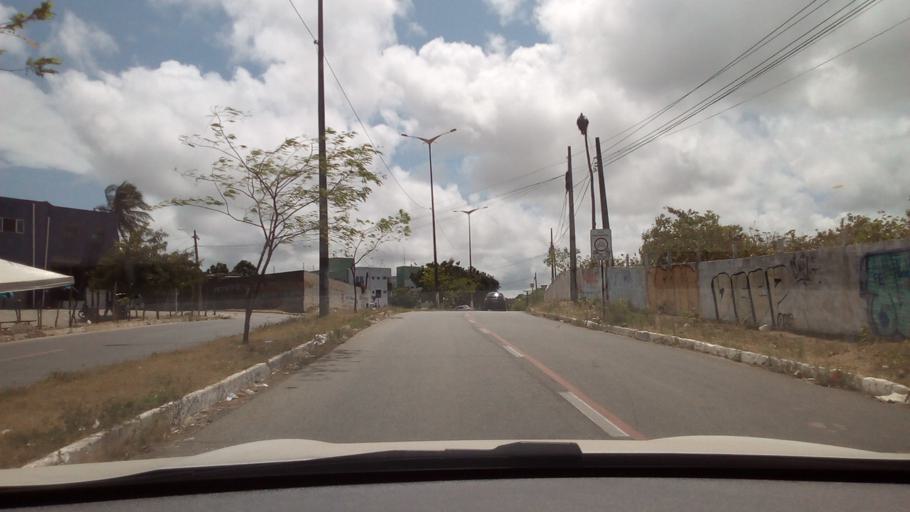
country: BR
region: Paraiba
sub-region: Joao Pessoa
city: Joao Pessoa
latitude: -7.1438
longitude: -34.8302
